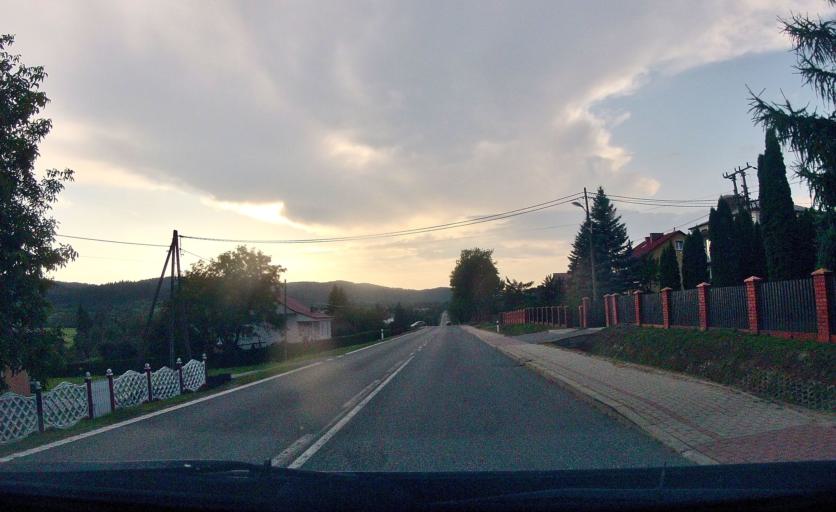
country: PL
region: Subcarpathian Voivodeship
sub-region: Powiat krosnienski
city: Dukla
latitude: 49.5610
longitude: 21.6121
